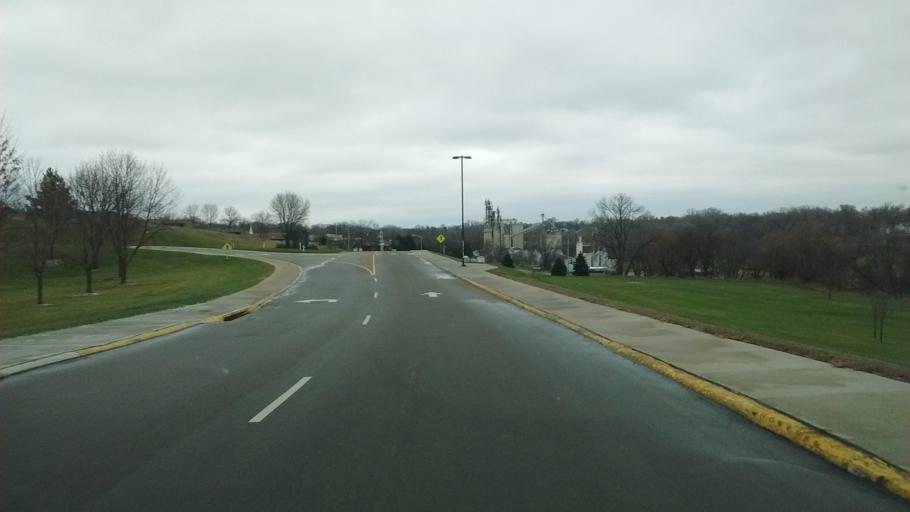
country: US
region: Iowa
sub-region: Woodbury County
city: Sioux City
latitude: 42.4815
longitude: -96.3491
